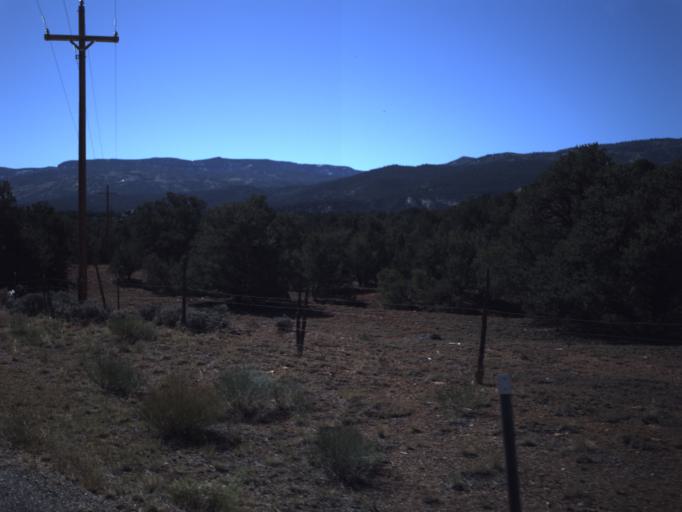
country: US
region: Utah
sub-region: Wayne County
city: Loa
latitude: 38.2508
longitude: -111.3783
